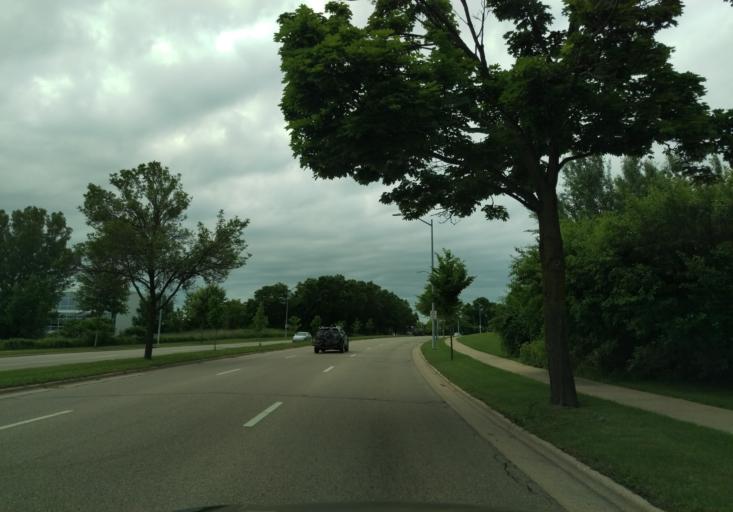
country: US
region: Wisconsin
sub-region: Dane County
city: Shorewood Hills
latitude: 43.0583
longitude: -89.4721
